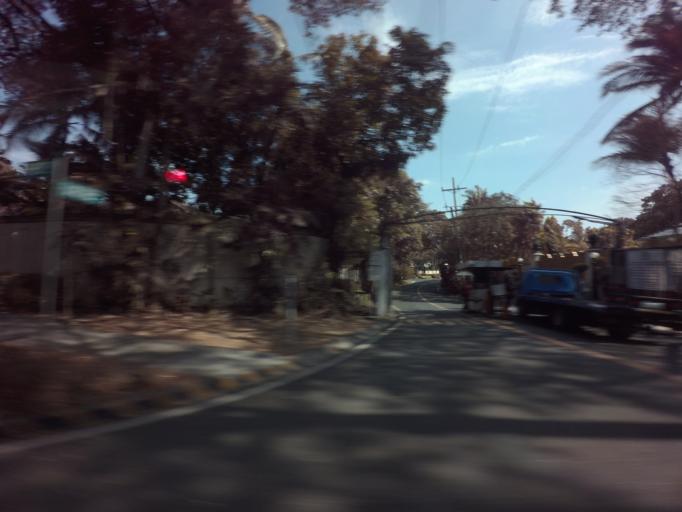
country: PH
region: Metro Manila
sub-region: Makati City
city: Makati City
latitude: 14.5474
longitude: 121.0382
